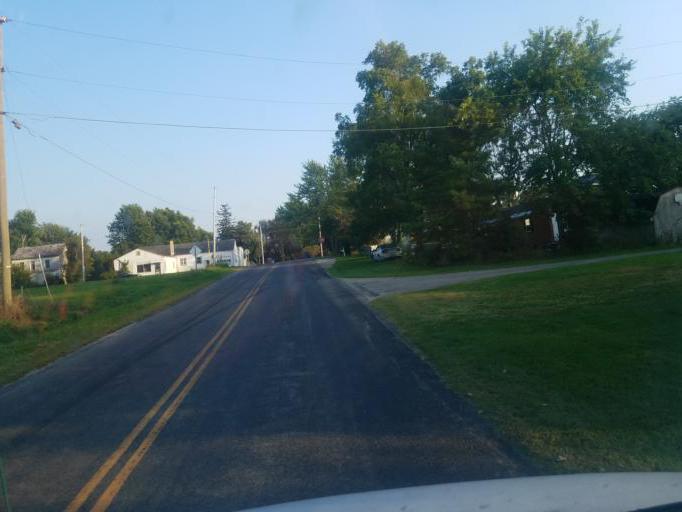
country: US
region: Ohio
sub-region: Crawford County
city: Bucyrus
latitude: 40.8726
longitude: -82.8759
